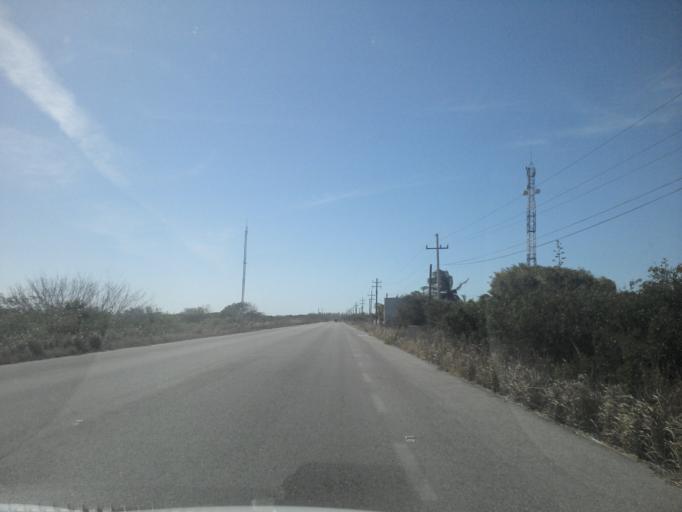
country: MX
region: Yucatan
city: Telchac Puerto
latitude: 21.3288
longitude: -89.3899
